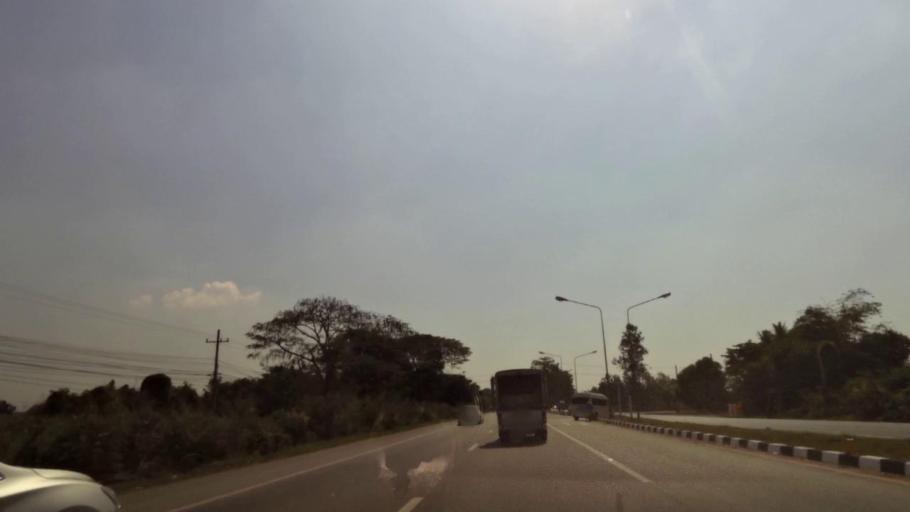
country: TH
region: Phichit
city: Bueng Na Rang
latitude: 16.1154
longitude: 100.1257
